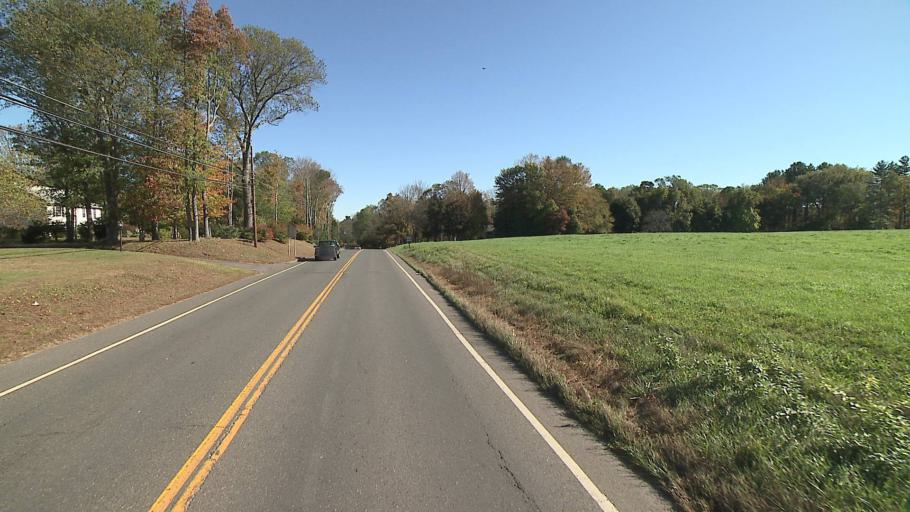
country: US
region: Connecticut
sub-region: Tolland County
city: South Coventry
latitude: 41.7039
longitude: -72.2980
